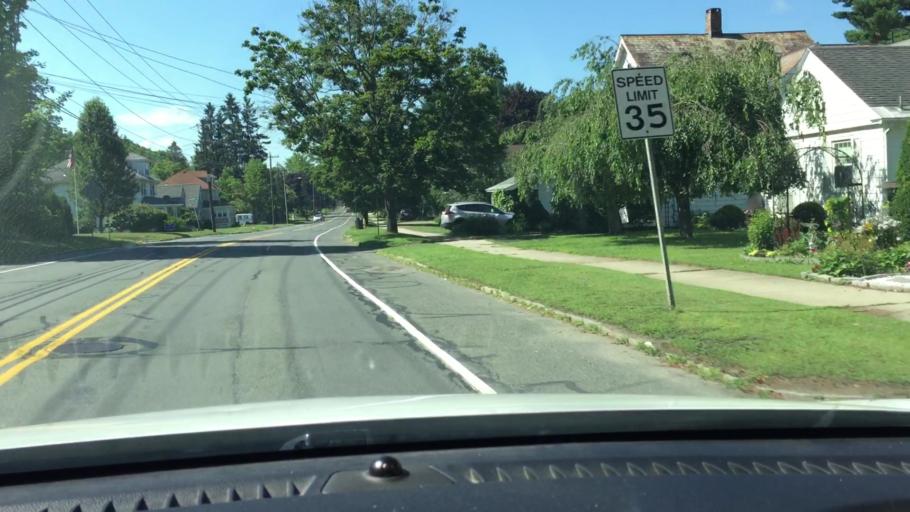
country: US
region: Massachusetts
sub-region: Berkshire County
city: Pittsfield
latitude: 42.4728
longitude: -73.2442
